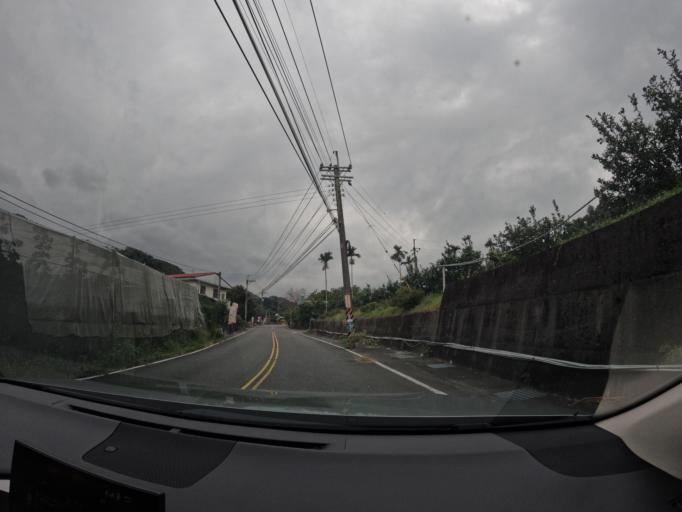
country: TW
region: Taiwan
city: Fengyuan
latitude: 24.3371
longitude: 120.8743
